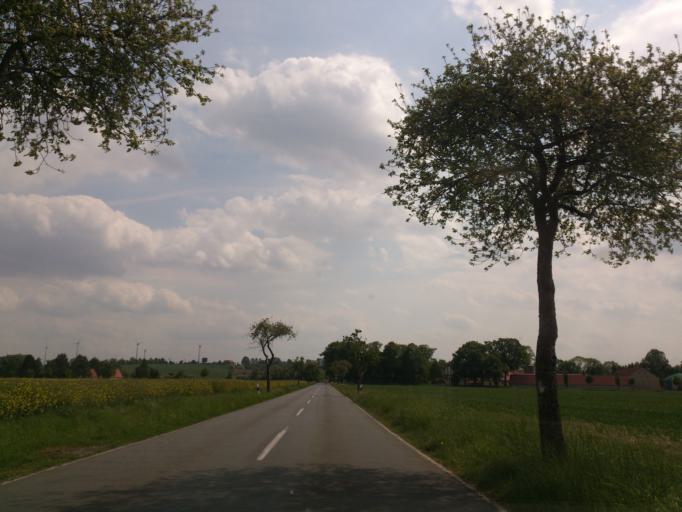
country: DE
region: North Rhine-Westphalia
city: Bad Lippspringe
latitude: 51.7615
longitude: 8.8217
